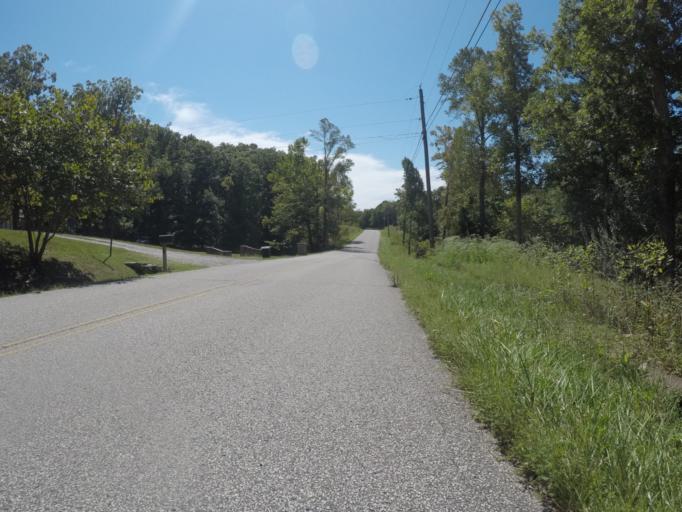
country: US
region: Kentucky
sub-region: Boyd County
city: Catlettsburg
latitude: 38.4103
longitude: -82.6544
